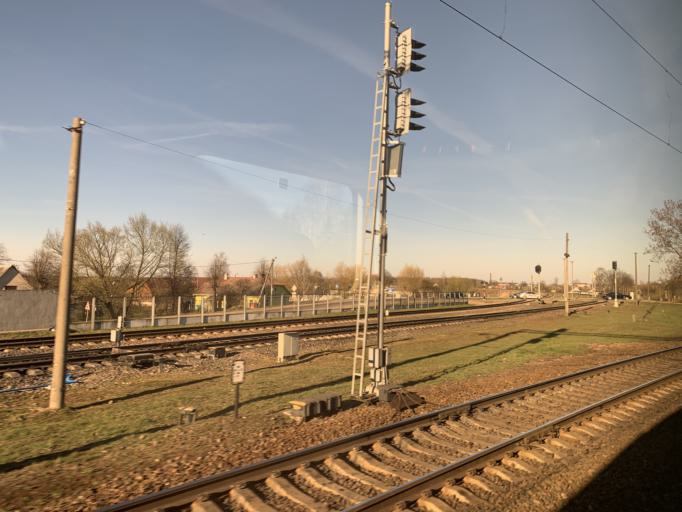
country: BY
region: Minsk
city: Maladzyechna
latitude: 54.3163
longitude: 26.8469
